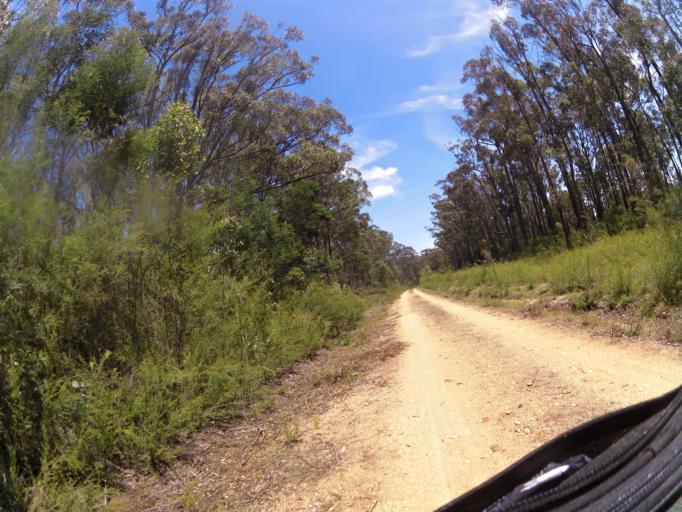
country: AU
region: Victoria
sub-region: East Gippsland
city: Lakes Entrance
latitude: -37.7586
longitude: 147.9564
